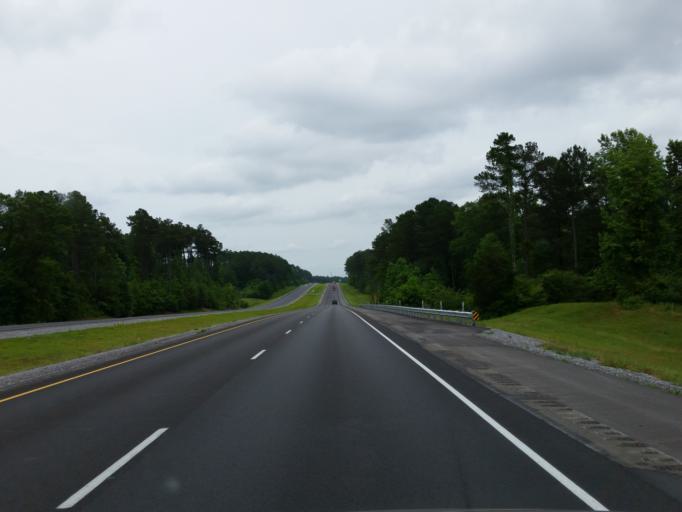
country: US
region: Mississippi
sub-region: Jones County
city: Sharon
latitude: 31.8889
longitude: -89.0350
